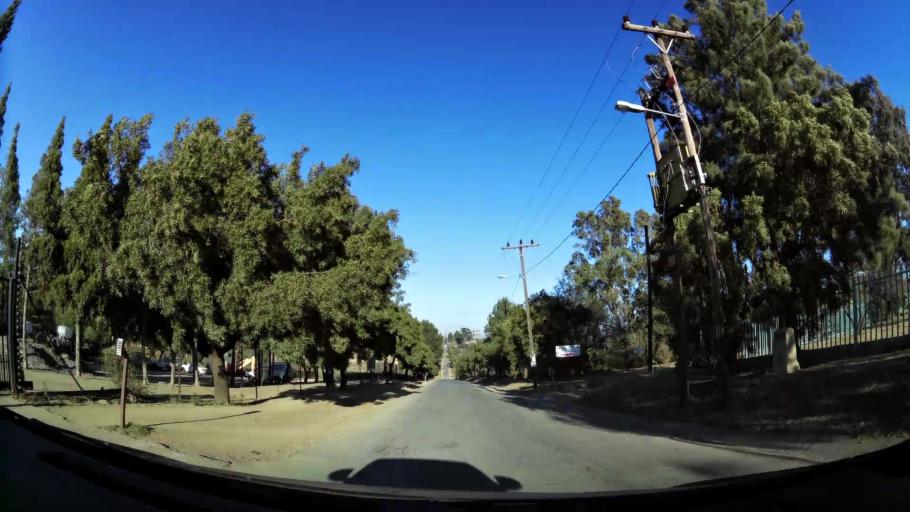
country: ZA
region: Gauteng
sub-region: City of Johannesburg Metropolitan Municipality
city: Midrand
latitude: -26.0316
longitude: 28.1486
